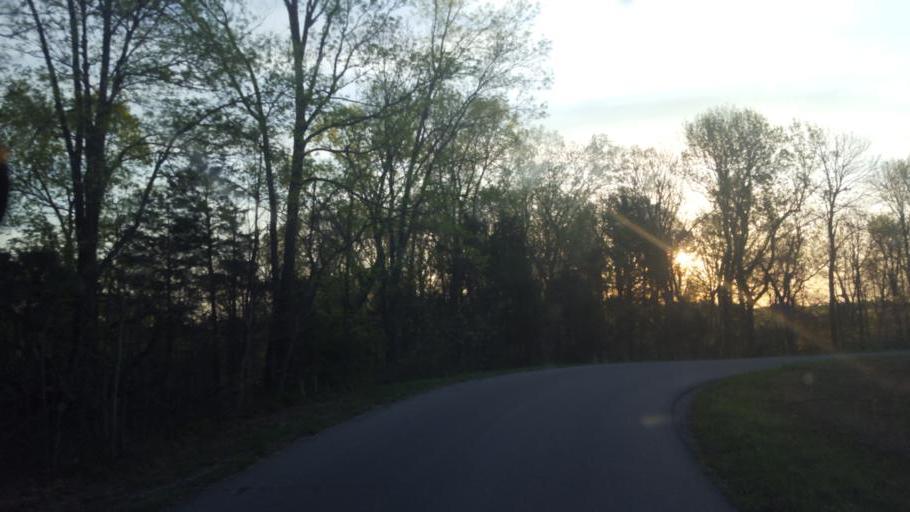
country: US
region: Kentucky
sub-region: Barren County
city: Cave City
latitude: 37.1427
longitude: -86.0228
